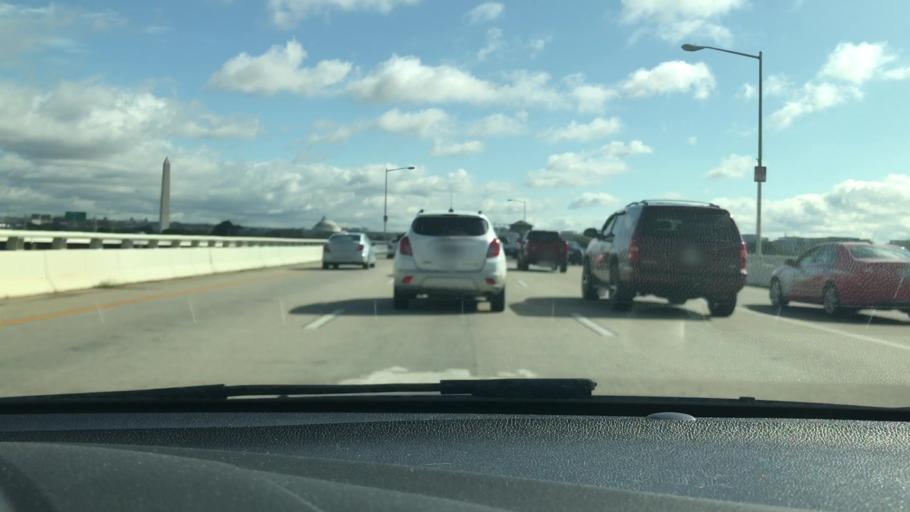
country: US
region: Washington, D.C.
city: Washington, D.C.
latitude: 38.8729
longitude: -77.0424
